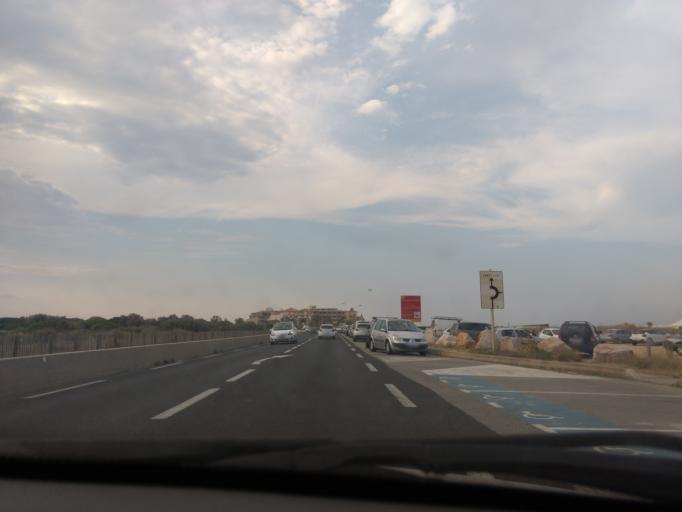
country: FR
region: Languedoc-Roussillon
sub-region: Departement des Pyrenees-Orientales
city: Canet-en-Roussillon
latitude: 42.6709
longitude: 3.0332
